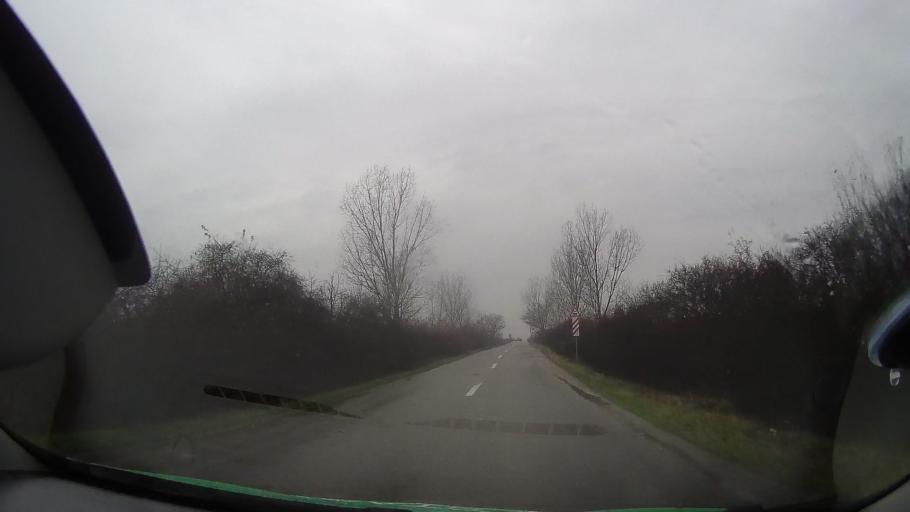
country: RO
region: Bihor
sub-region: Comuna Tinca
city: Tinca
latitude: 46.7720
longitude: 21.8958
